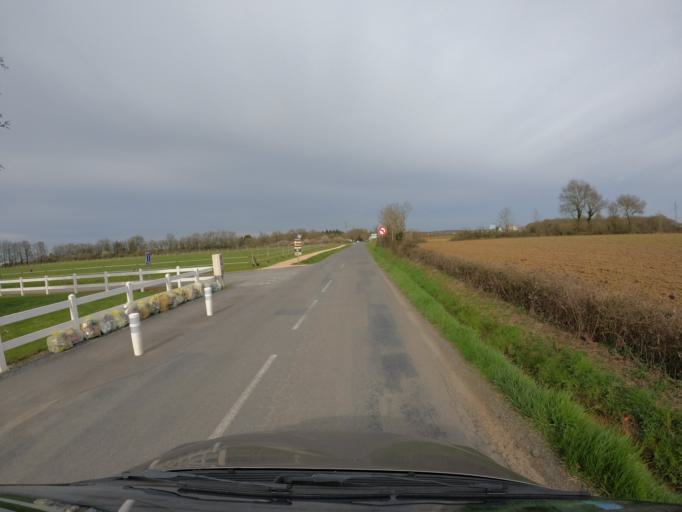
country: FR
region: Pays de la Loire
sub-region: Departement de la Vendee
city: Bouffere
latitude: 46.9592
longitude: -1.3232
